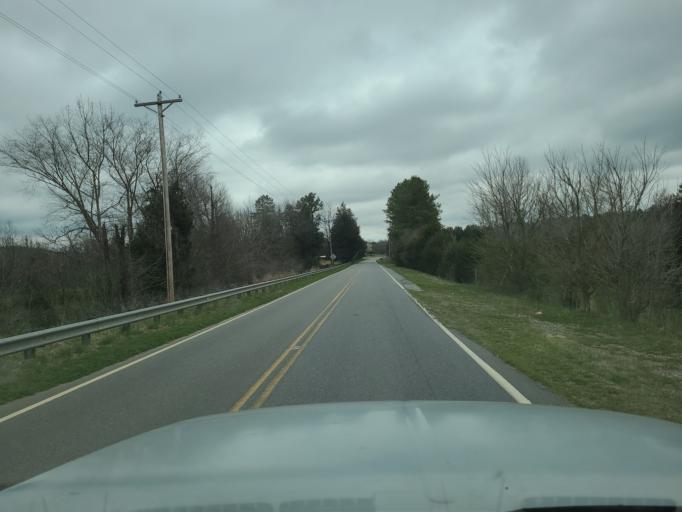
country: US
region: North Carolina
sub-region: Cleveland County
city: Shelby
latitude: 35.4488
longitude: -81.6427
